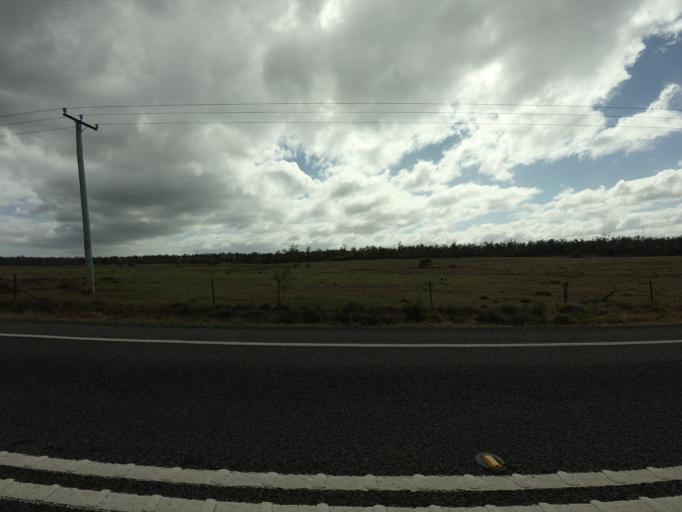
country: AU
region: Tasmania
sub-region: Northern Midlands
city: Evandale
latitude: -41.8310
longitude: 147.4848
